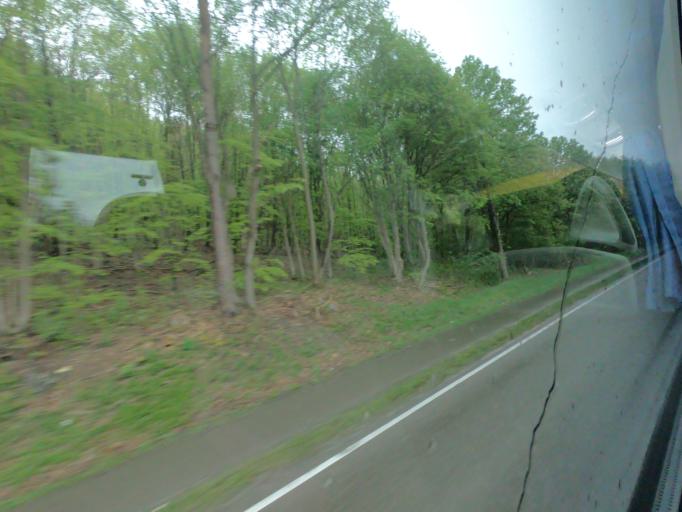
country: DE
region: Baden-Wuerttemberg
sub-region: Regierungsbezirk Stuttgart
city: Konigsbronn
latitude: 48.7473
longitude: 10.1054
